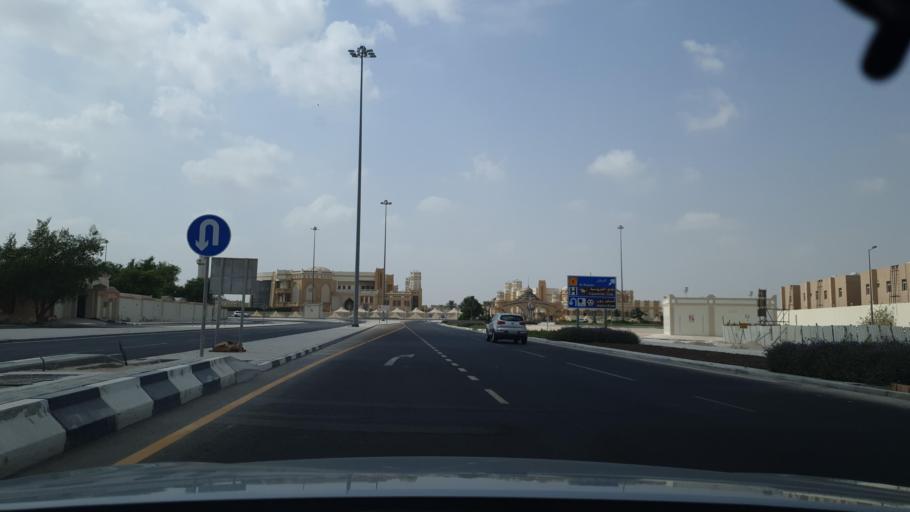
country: QA
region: Baladiyat ar Rayyan
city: Ar Rayyan
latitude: 25.2720
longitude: 51.4335
